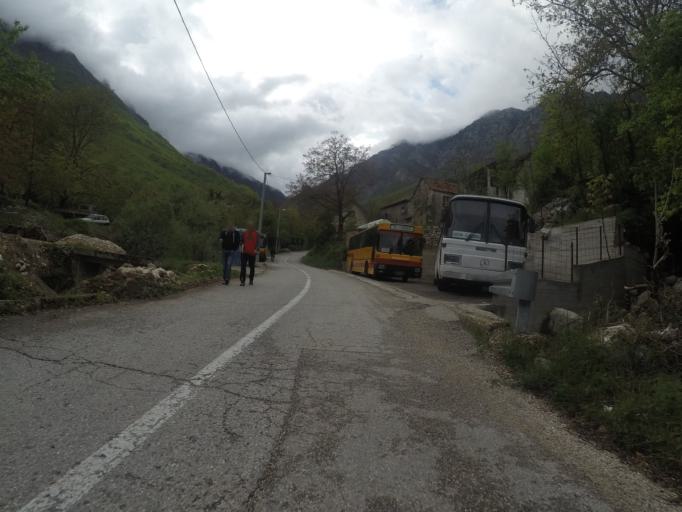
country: BA
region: Federation of Bosnia and Herzegovina
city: Kocerin
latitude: 43.5440
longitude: 17.5486
